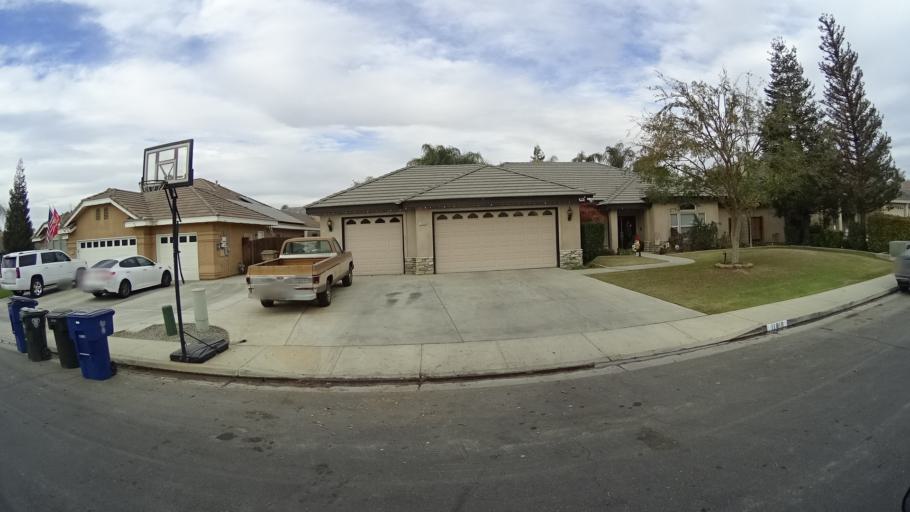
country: US
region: California
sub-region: Kern County
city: Rosedale
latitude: 35.4148
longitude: -119.1345
